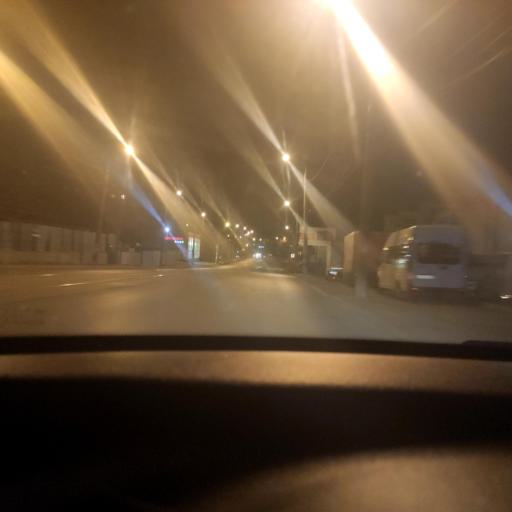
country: RU
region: Samara
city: Samara
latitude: 53.1932
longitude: 50.1652
